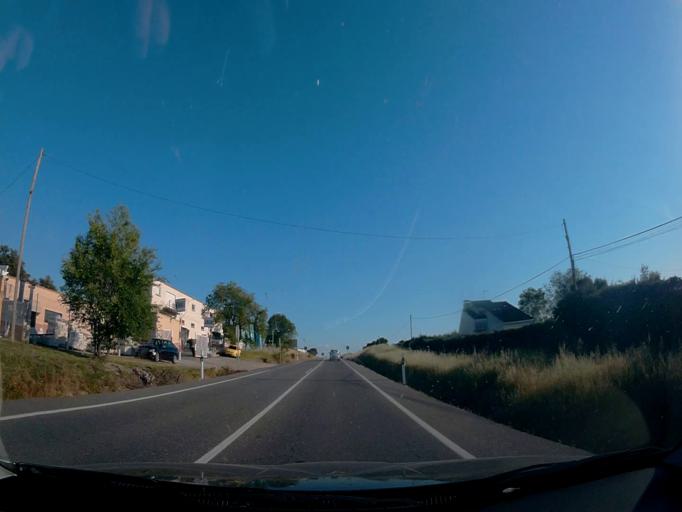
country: ES
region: Castille-La Mancha
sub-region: Province of Toledo
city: Escalona
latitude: 40.1318
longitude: -4.4050
